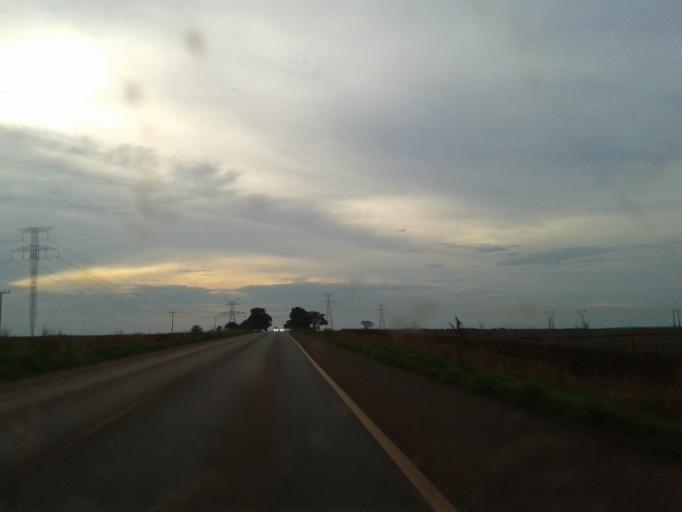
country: BR
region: Goias
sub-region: Santa Helena De Goias
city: Santa Helena de Goias
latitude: -17.9093
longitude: -50.6251
